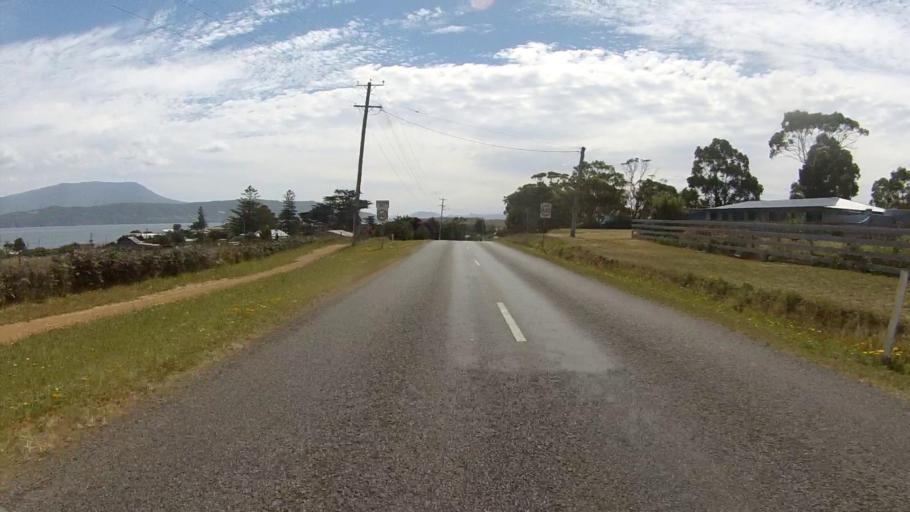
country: AU
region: Tasmania
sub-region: Kingborough
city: Taroona
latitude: -42.9975
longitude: 147.4041
